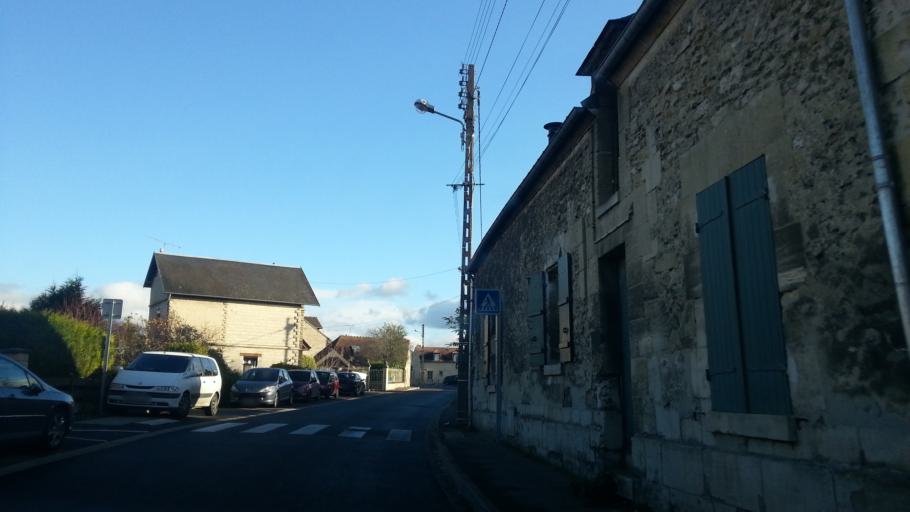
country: FR
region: Picardie
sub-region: Departement de l'Oise
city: Verneuil-en-Halatte
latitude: 49.2784
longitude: 2.5113
